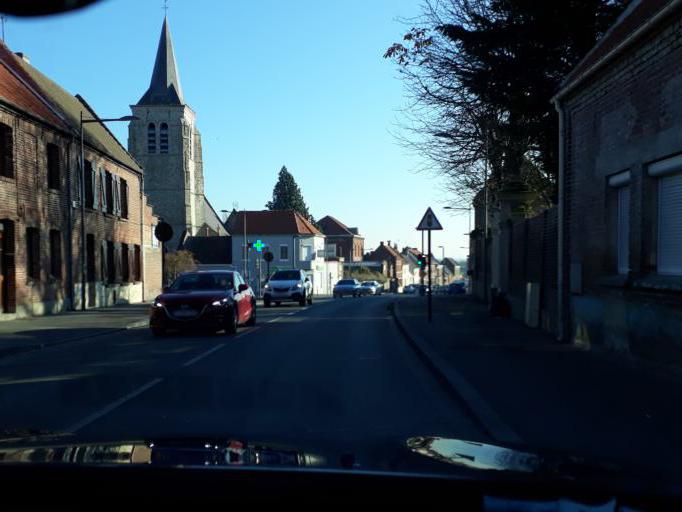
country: FR
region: Nord-Pas-de-Calais
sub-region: Departement du Nord
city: Lewarde
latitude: 50.3410
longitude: 3.1690
